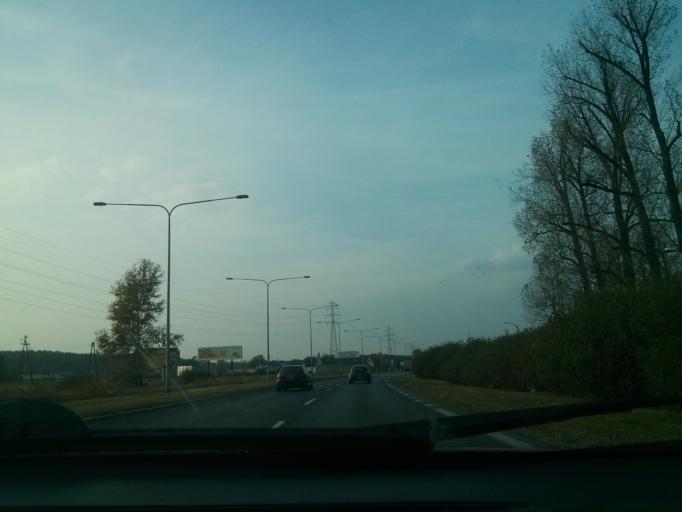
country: PL
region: Masovian Voivodeship
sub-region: Warszawa
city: Kabaty
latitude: 52.1196
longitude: 21.1014
